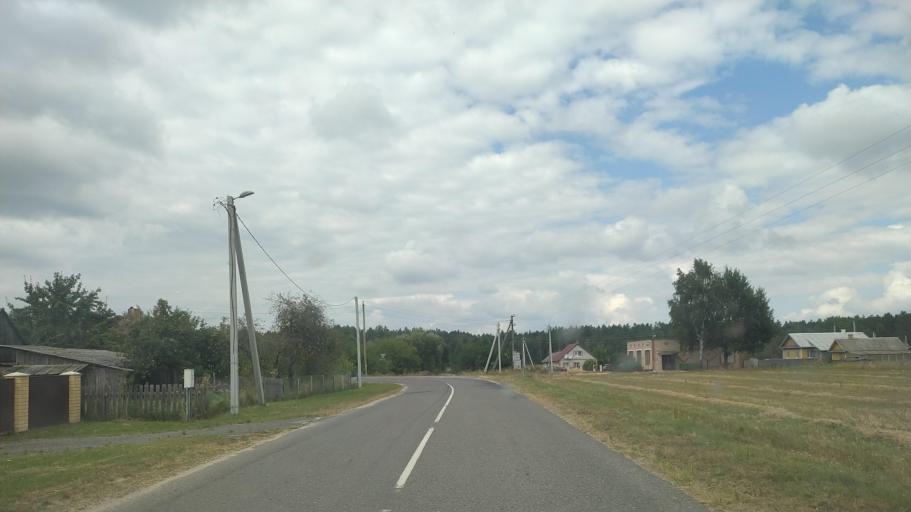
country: BY
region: Brest
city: Byelaazyorsk
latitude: 52.5429
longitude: 25.1112
